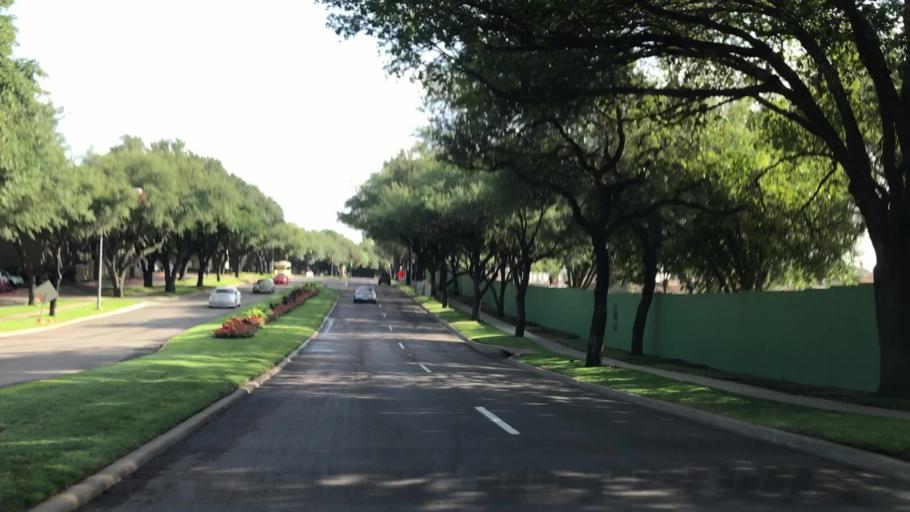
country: US
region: Texas
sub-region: Dallas County
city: University Park
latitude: 32.8583
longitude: -96.7652
